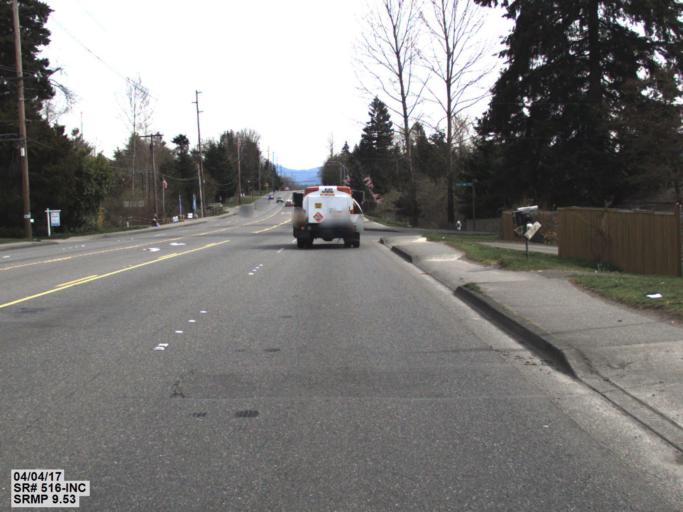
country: US
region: Washington
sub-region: King County
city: Lea Hill
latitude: 47.3580
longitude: -122.1622
